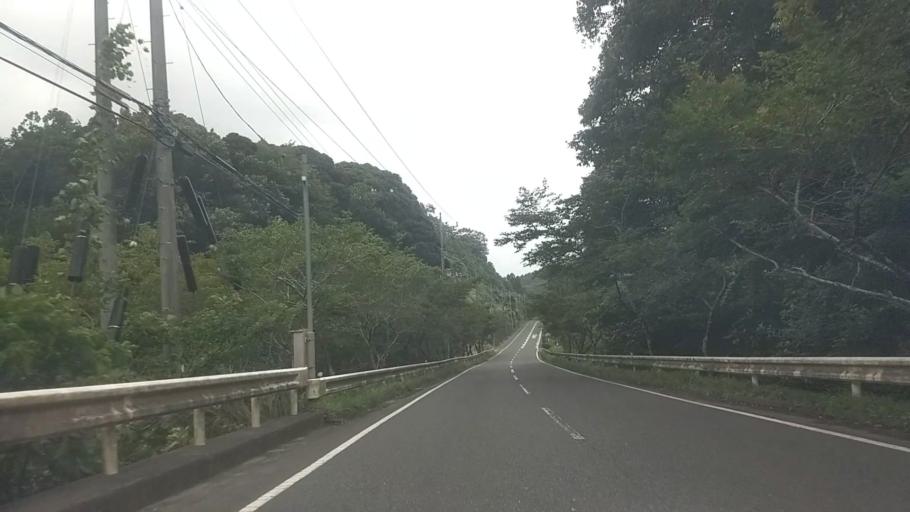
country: JP
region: Chiba
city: Kimitsu
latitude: 35.2329
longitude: 139.9676
